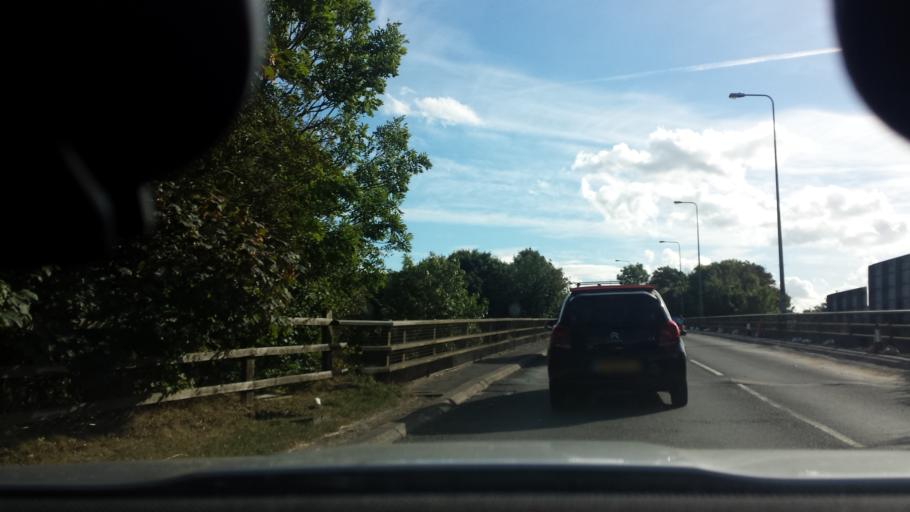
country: GB
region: England
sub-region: Kent
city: Swanley
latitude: 51.3900
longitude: 0.1881
